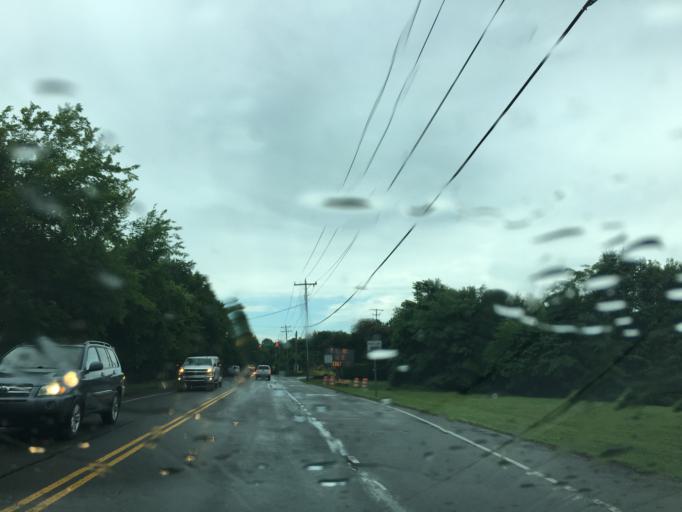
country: US
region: Tennessee
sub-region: Davidson County
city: Belle Meade
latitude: 36.0582
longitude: -86.9454
